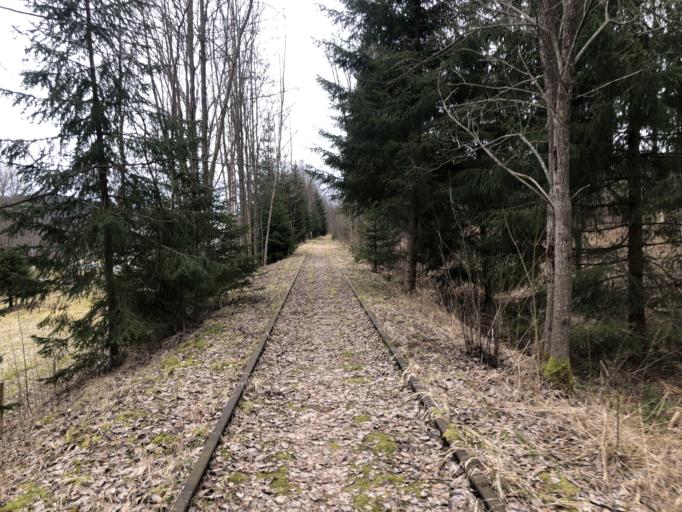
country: SE
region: Vaermland
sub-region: Filipstads Kommun
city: Lesjofors
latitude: 59.9704
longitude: 14.1895
